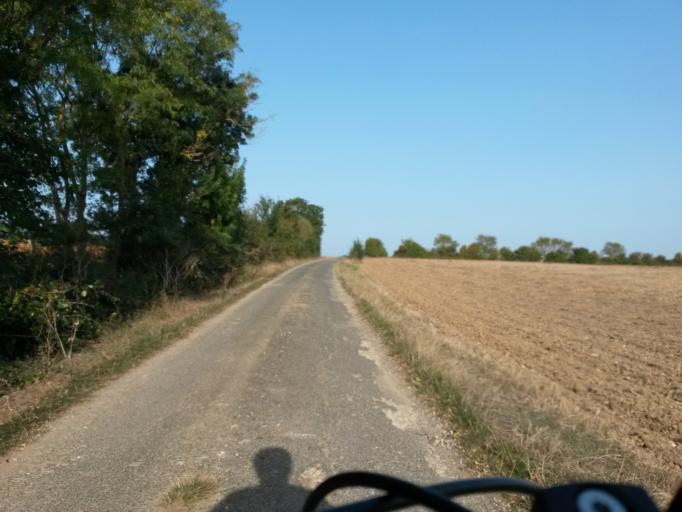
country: FR
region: Poitou-Charentes
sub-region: Departement de la Charente-Maritime
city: Saint-Xandre
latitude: 46.2234
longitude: -1.1129
